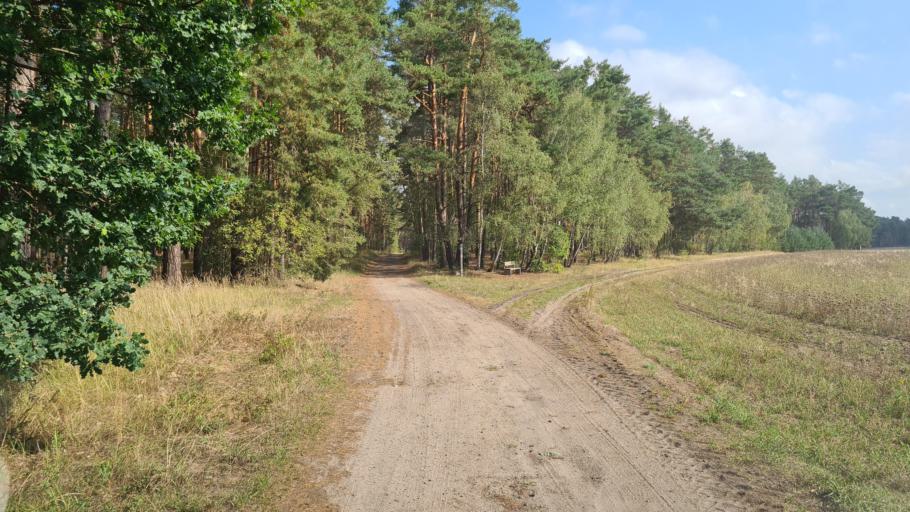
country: DE
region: Brandenburg
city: Belzig
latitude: 52.1564
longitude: 12.6526
